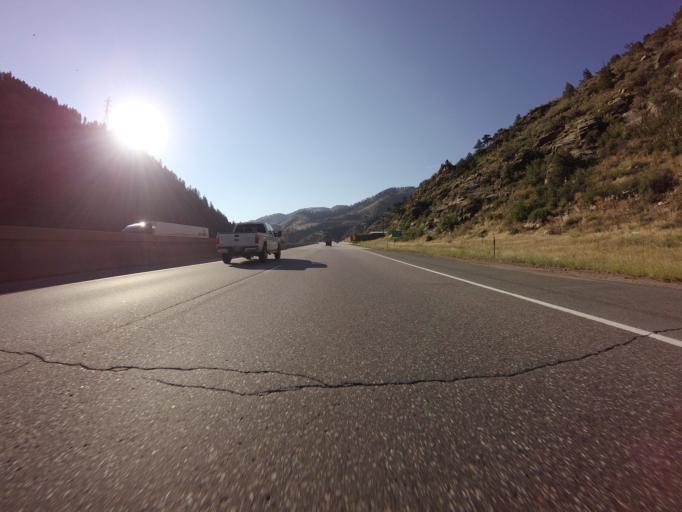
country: US
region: Colorado
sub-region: Clear Creek County
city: Idaho Springs
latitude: 39.7442
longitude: -105.4557
